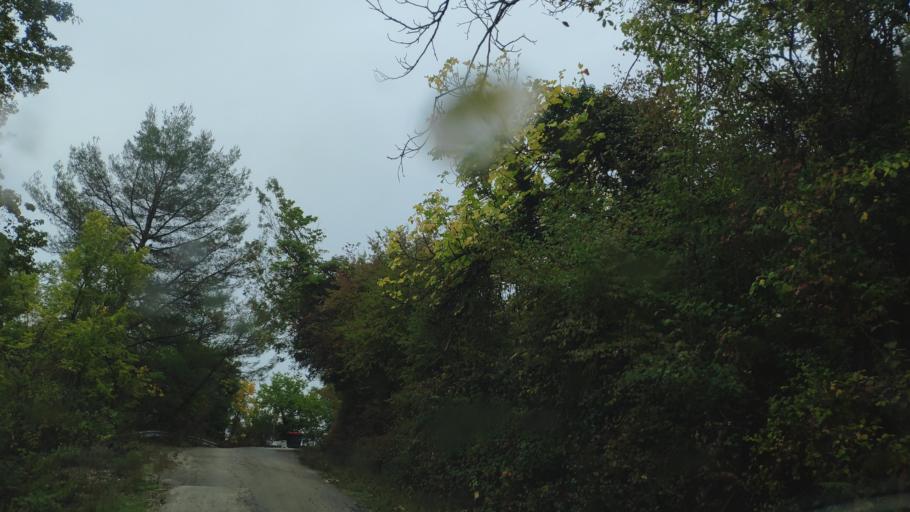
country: GR
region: Epirus
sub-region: Nomos Thesprotias
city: Paramythia
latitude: 39.4629
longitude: 20.6711
